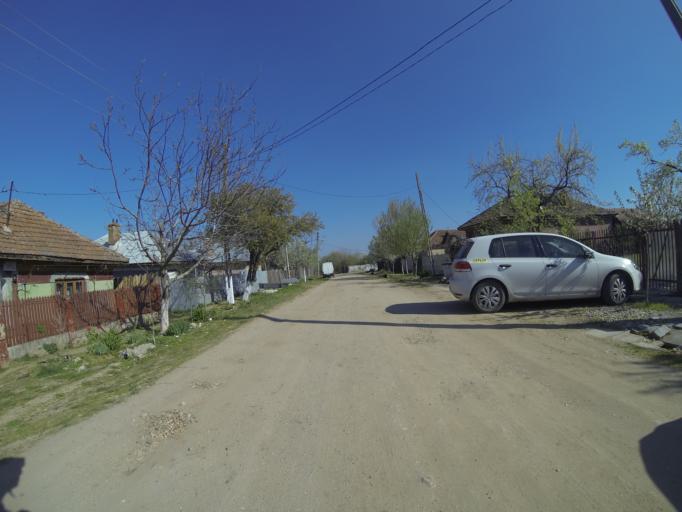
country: RO
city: Varvoru
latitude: 44.2236
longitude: 23.6292
